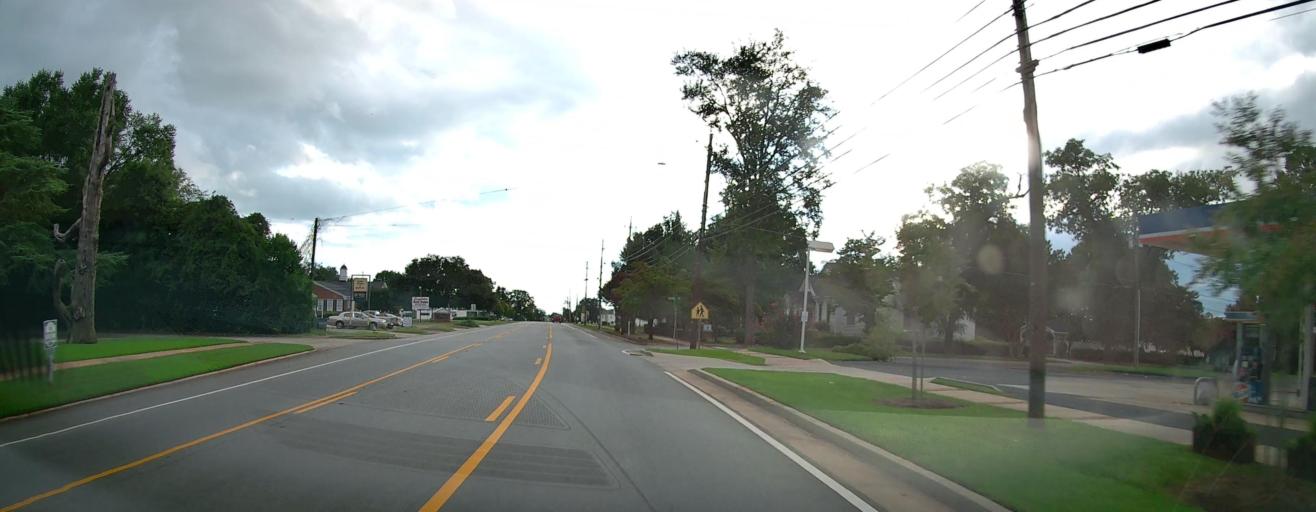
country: US
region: Georgia
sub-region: Houston County
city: Perry
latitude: 32.4596
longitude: -83.7271
